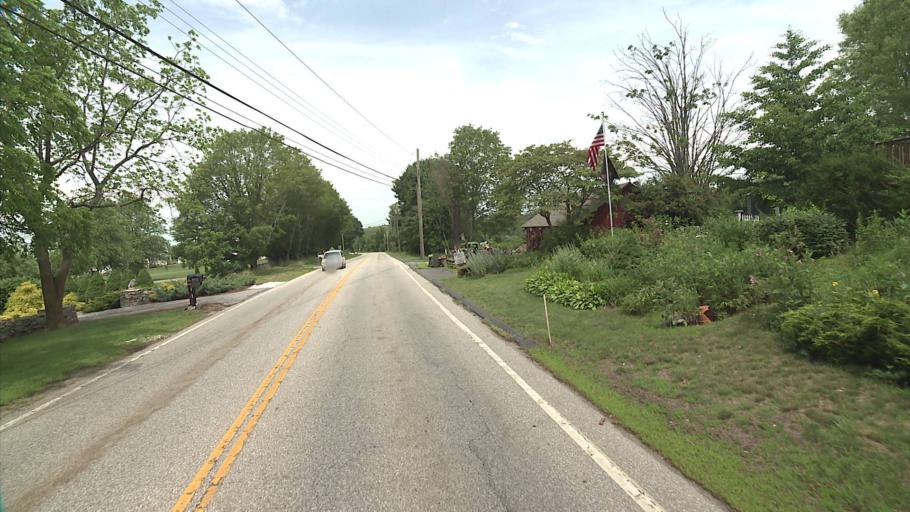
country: US
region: Connecticut
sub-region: New London County
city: Preston City
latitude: 41.5451
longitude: -71.9674
